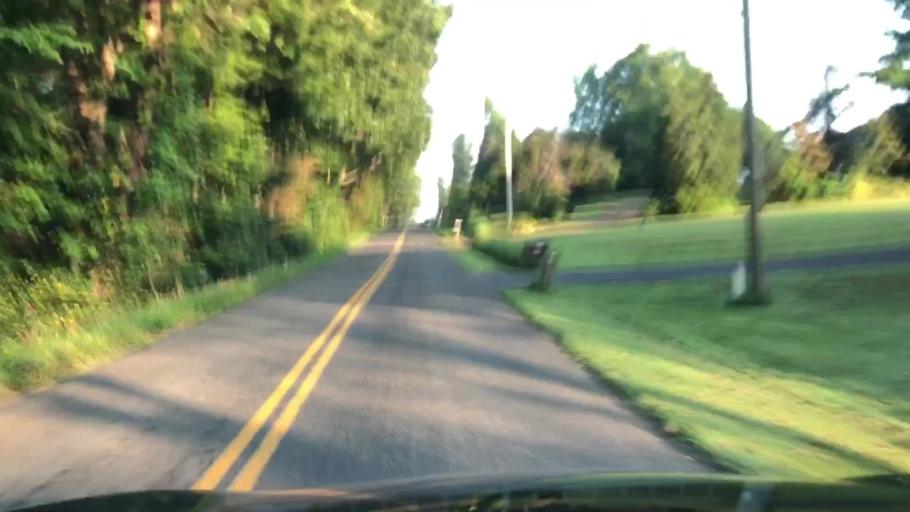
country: US
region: Virginia
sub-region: Fauquier County
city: New Baltimore
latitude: 38.7298
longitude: -77.6635
